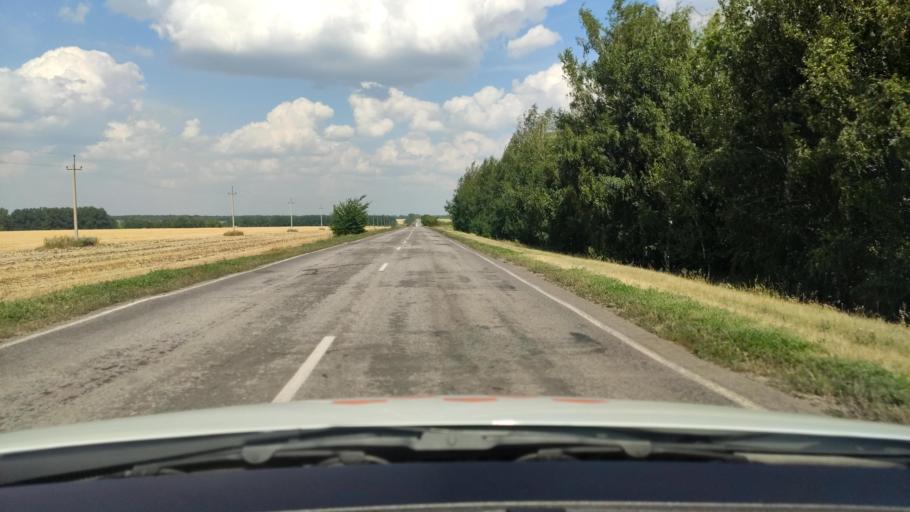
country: RU
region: Voronezj
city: Pereleshinskiy
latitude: 51.7380
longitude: 40.3926
